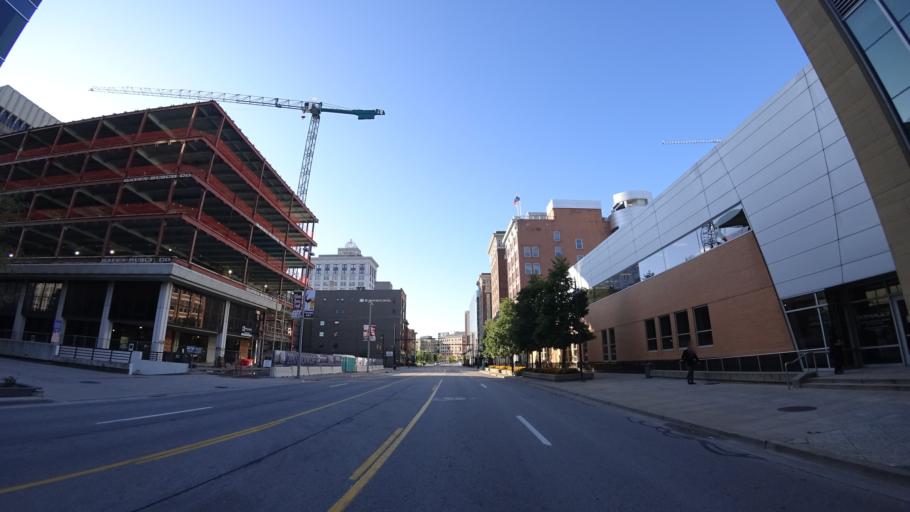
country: US
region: Michigan
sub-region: Kent County
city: Grand Rapids
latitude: 42.9680
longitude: -85.6722
